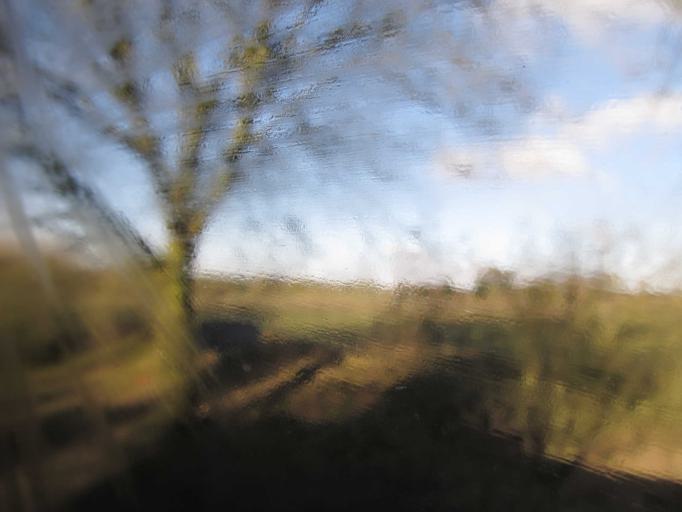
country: GB
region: England
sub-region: Hampshire
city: Kings Worthy
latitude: 51.1652
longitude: -1.3178
